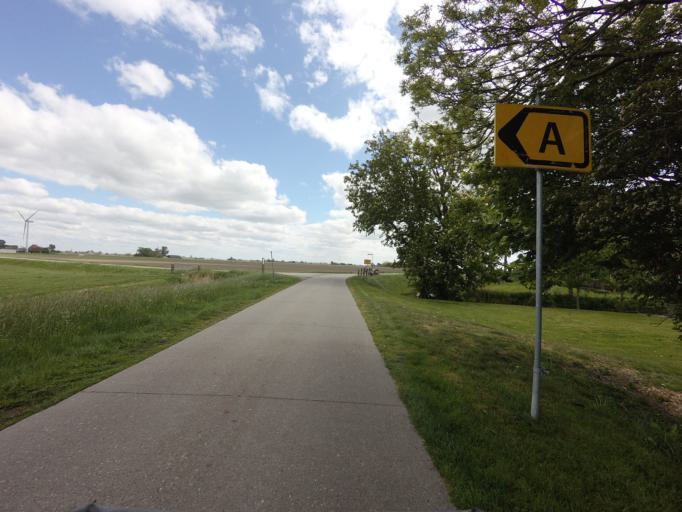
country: NL
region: Friesland
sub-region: Gemeente Littenseradiel
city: Wommels
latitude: 53.1192
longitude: 5.5522
